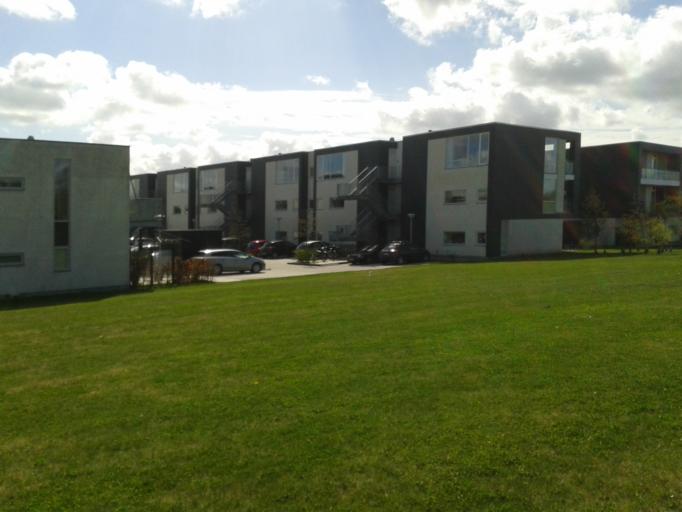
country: DK
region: North Denmark
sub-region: Alborg Kommune
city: Gistrup
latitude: 57.0121
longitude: 9.9621
